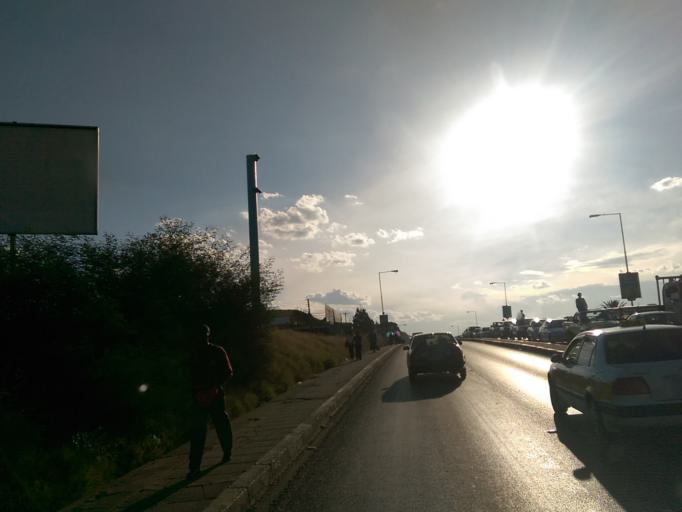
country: LS
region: Maseru
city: Maseru
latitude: -29.3135
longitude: 27.5078
